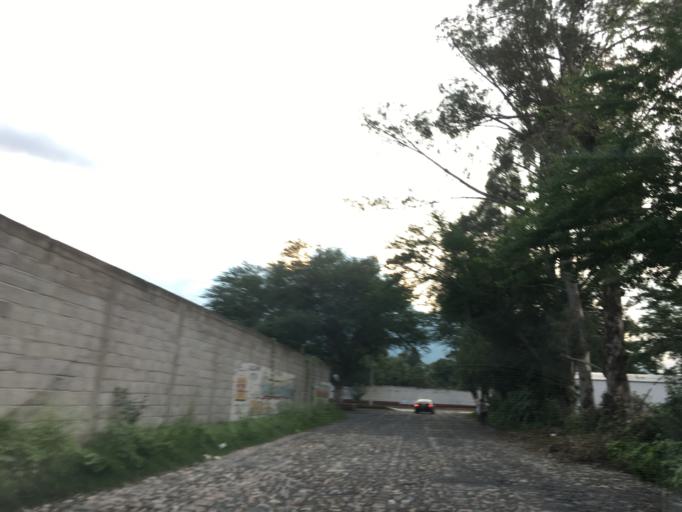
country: MX
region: Nayarit
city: Jala
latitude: 21.0993
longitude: -104.4373
